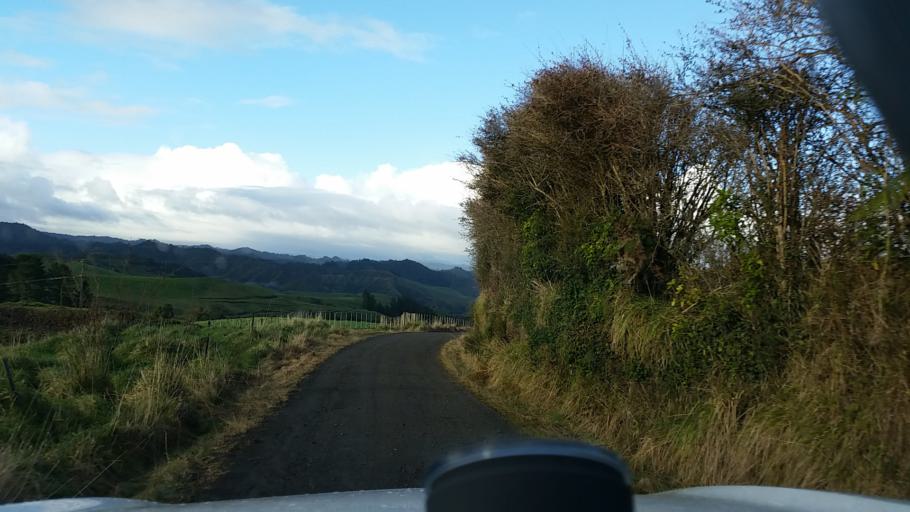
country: NZ
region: Taranaki
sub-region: South Taranaki District
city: Eltham
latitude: -39.4089
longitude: 174.5702
